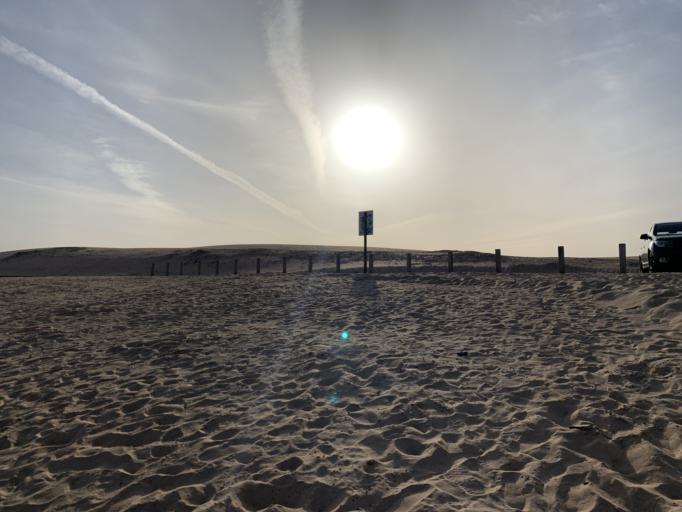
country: ES
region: Canary Islands
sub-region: Provincia de Las Palmas
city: Corralejo
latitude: 28.6713
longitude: -13.8333
